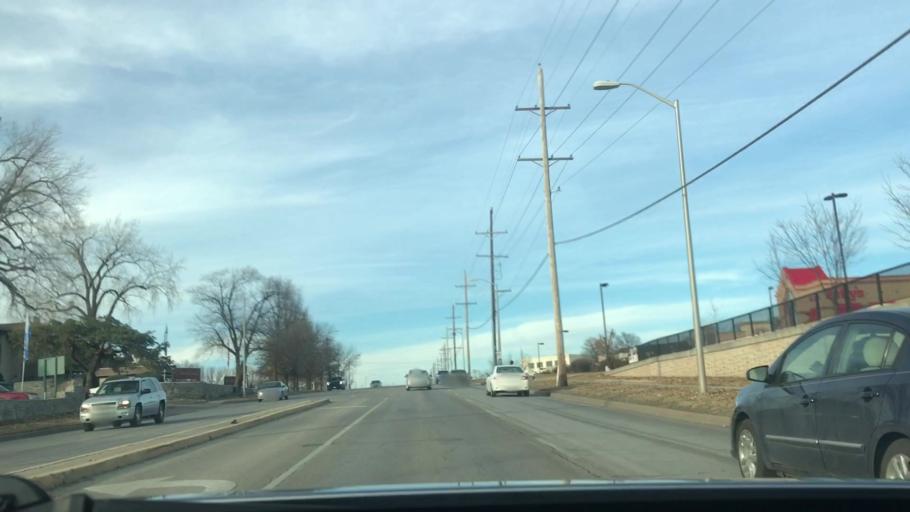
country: US
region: Missouri
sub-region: Clay County
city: Gladstone
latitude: 39.1835
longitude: -94.5766
